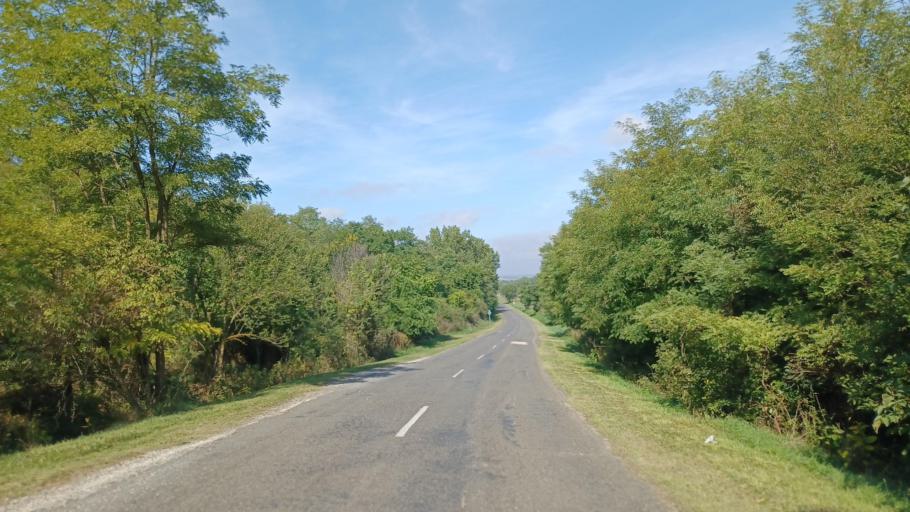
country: HU
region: Tolna
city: Pincehely
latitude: 46.6824
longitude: 18.4631
